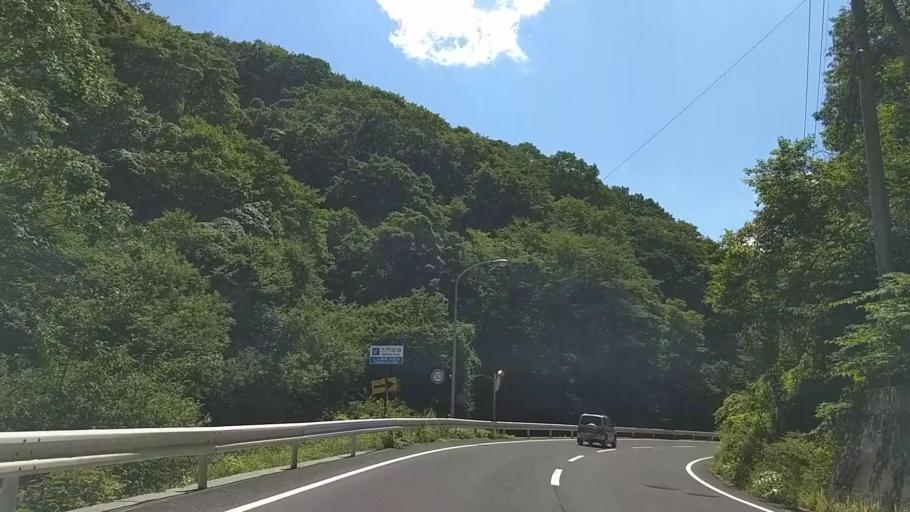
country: JP
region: Nagano
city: Chino
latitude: 36.0942
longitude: 138.2240
